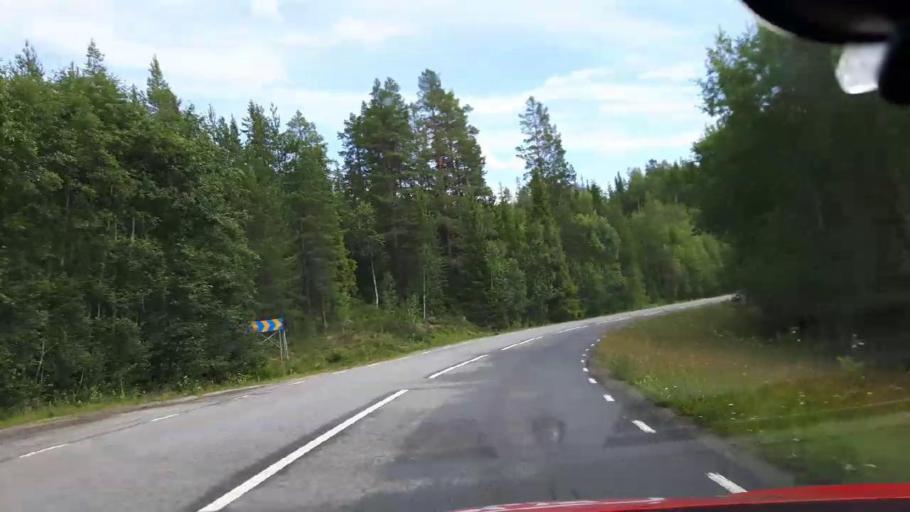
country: SE
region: Jaemtland
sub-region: Stroemsunds Kommun
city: Stroemsund
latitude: 64.3431
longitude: 14.9432
